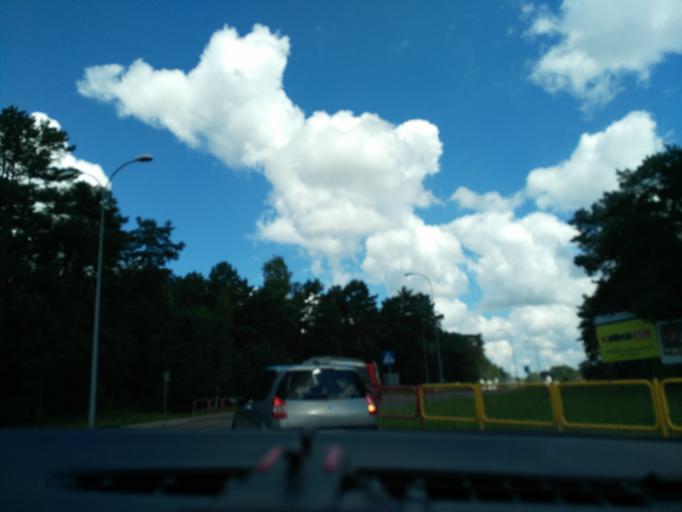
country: PL
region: Podlasie
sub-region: Powiat siemiatycki
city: Siemiatycze
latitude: 52.3937
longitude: 22.8705
